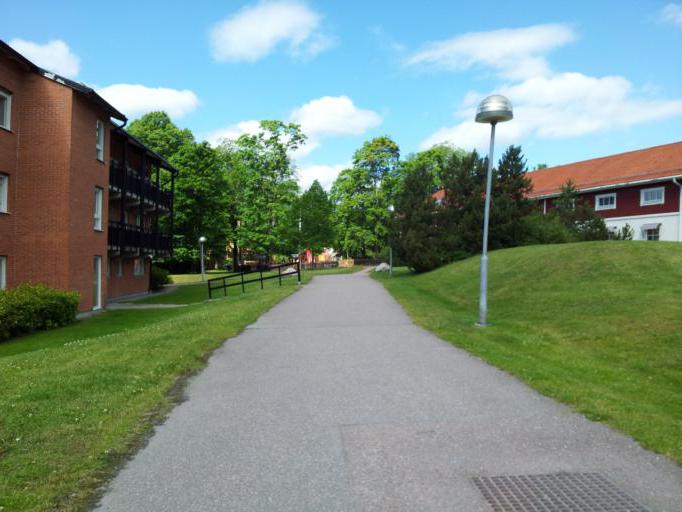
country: SE
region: Uppsala
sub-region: Uppsala Kommun
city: Uppsala
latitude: 59.8776
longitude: 17.6437
